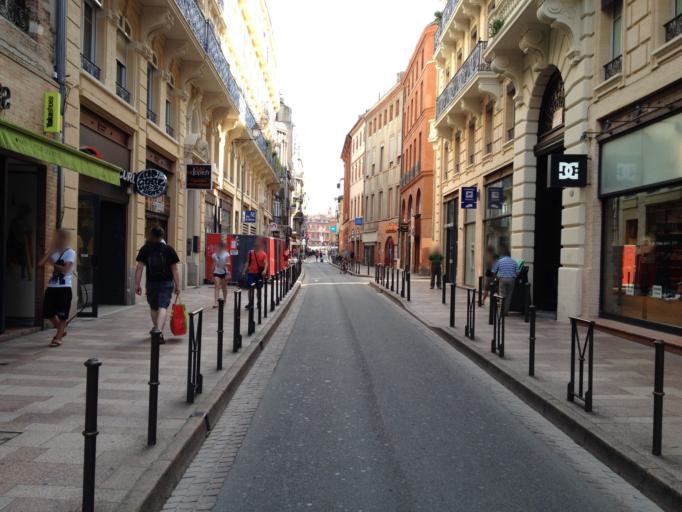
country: FR
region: Midi-Pyrenees
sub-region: Departement de la Haute-Garonne
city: Toulouse
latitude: 43.6066
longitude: 1.4448
